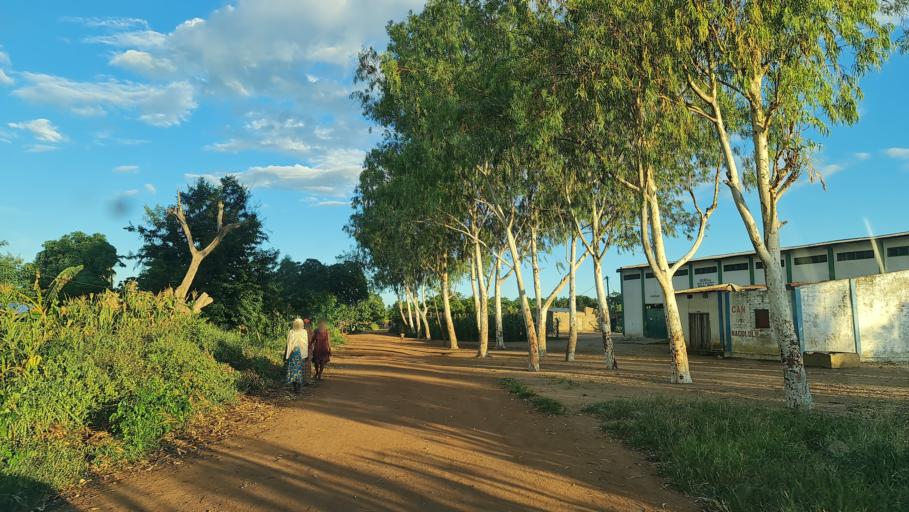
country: MZ
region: Nampula
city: Ilha de Mocambique
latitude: -14.9022
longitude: 40.1379
